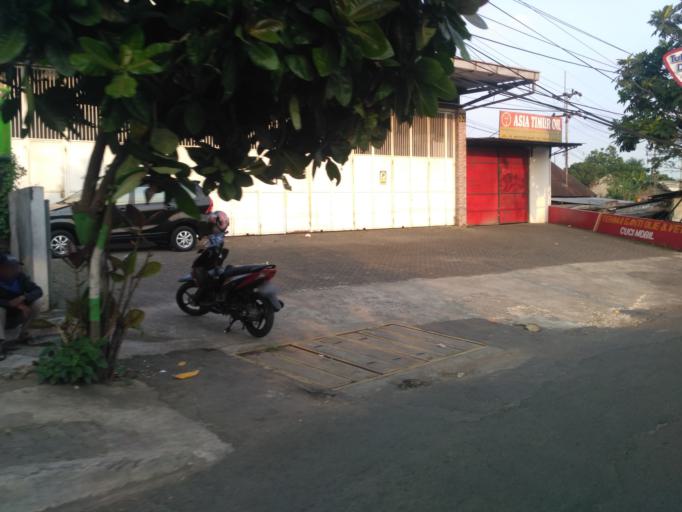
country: ID
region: East Java
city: Kepuh
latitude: -8.0020
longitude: 112.6178
